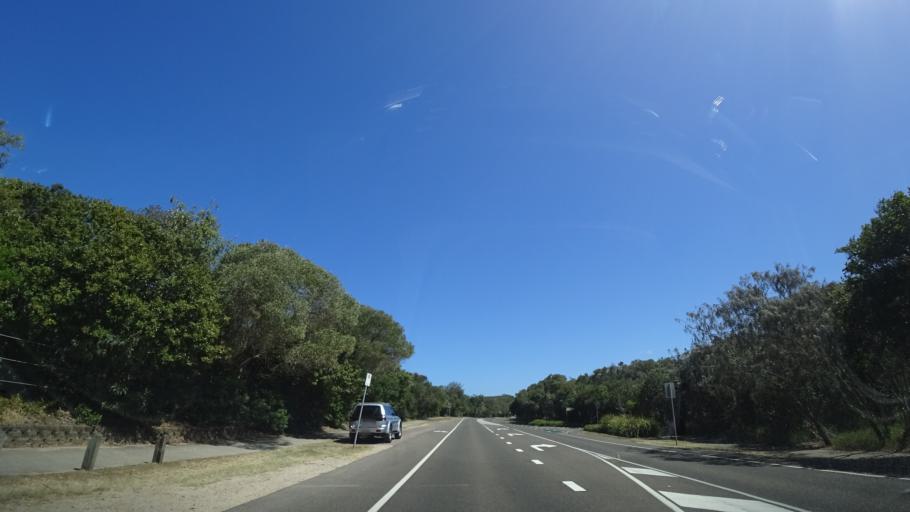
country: AU
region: Queensland
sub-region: Sunshine Coast
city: Mooloolaba
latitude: -26.6083
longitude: 153.0989
